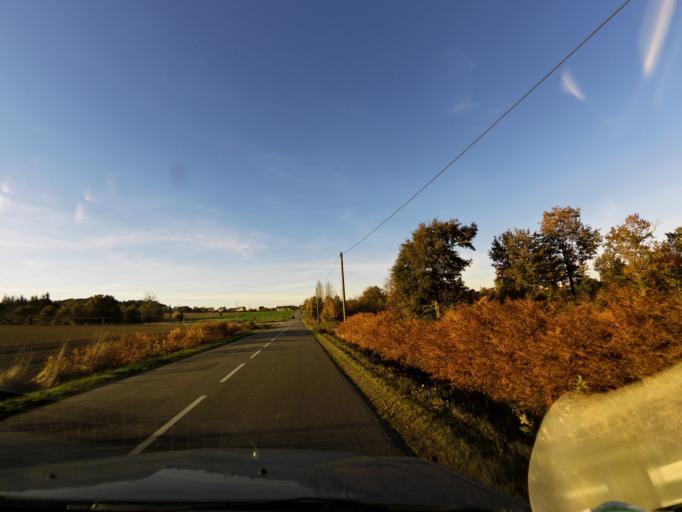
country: FR
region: Brittany
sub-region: Departement d'Ille-et-Vilaine
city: Chanteloup
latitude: 47.9412
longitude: -1.6044
